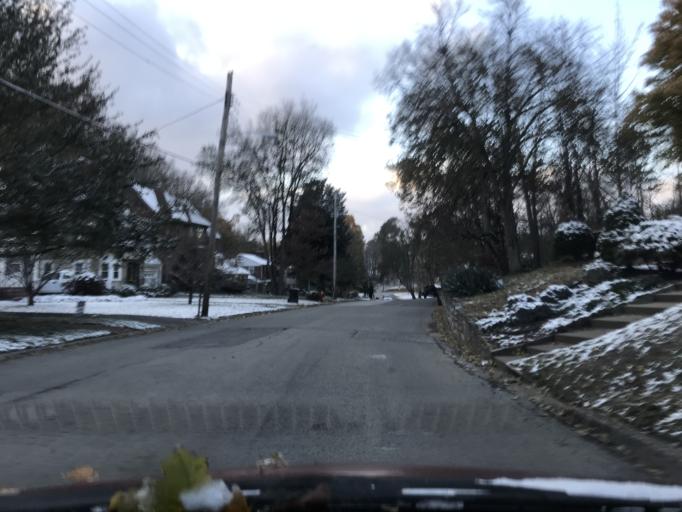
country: US
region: Kentucky
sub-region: Jefferson County
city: Indian Hills
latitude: 38.2573
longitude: -85.6962
